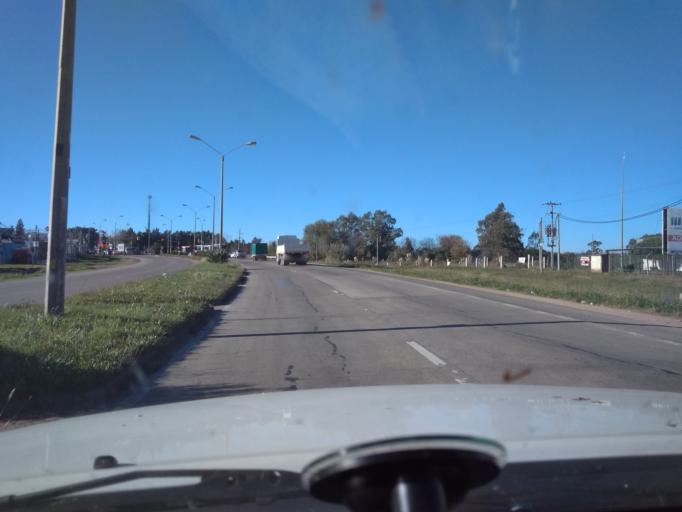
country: UY
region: Canelones
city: Joaquin Suarez
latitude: -34.7718
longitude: -56.0265
